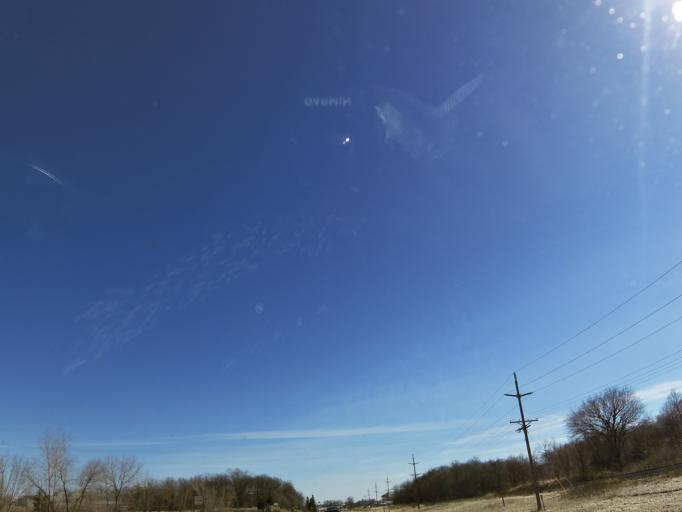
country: US
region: Minnesota
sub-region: Wright County
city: Buffalo
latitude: 45.1885
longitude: -93.8853
